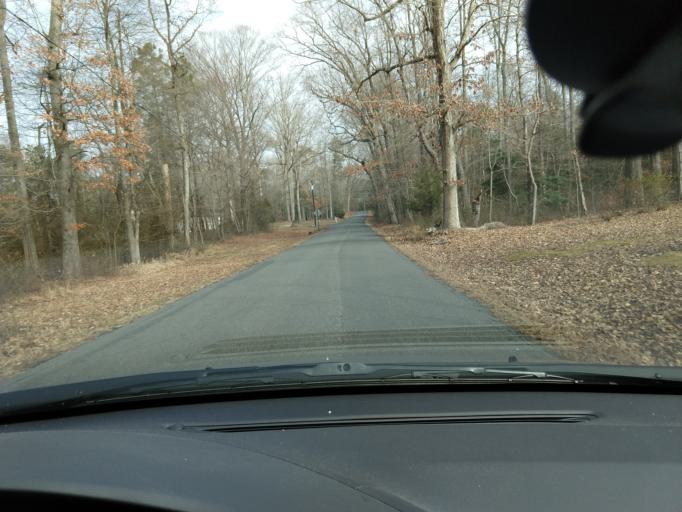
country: US
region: Virginia
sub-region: Henrico County
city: Fort Lee
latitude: 37.4384
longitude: -77.2551
